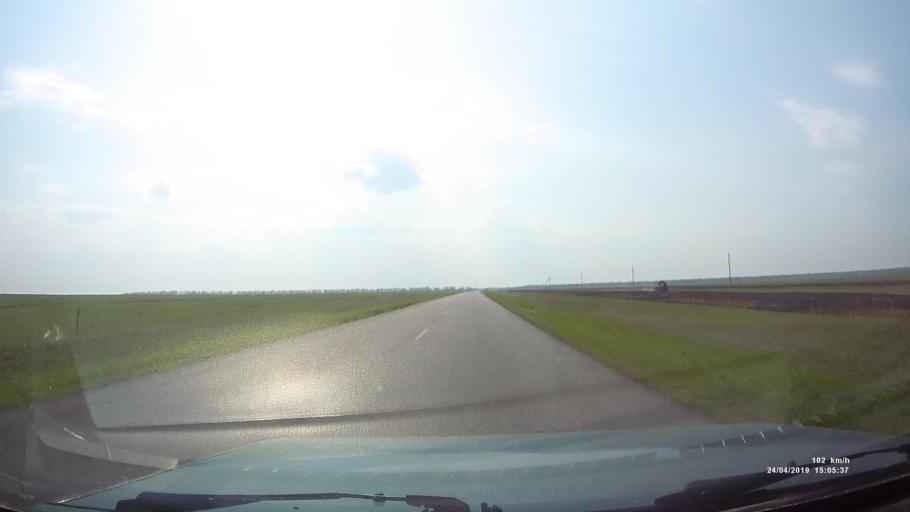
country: RU
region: Rostov
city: Remontnoye
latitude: 46.5599
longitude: 43.4450
